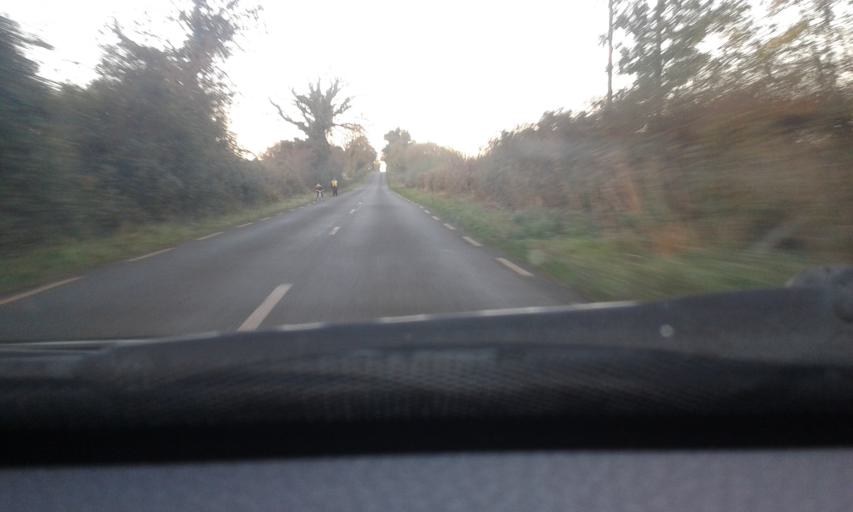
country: IE
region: Leinster
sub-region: Kildare
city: Monasterevin
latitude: 53.1647
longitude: -7.0364
